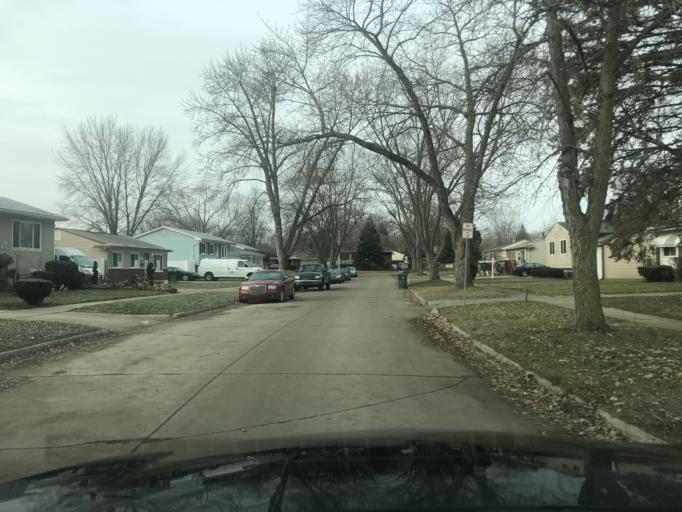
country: US
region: Michigan
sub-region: Wayne County
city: Taylor
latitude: 42.1904
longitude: -83.3168
